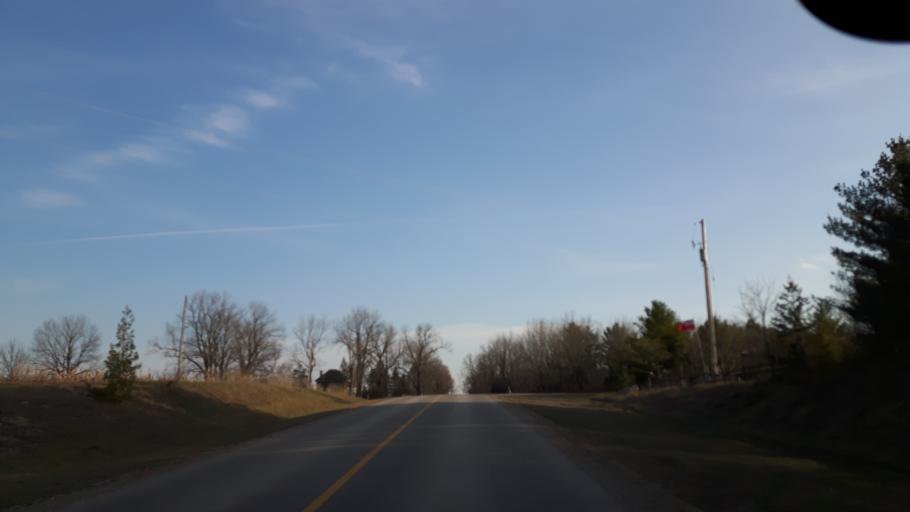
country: CA
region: Ontario
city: Goderich
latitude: 43.6704
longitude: -81.6644
